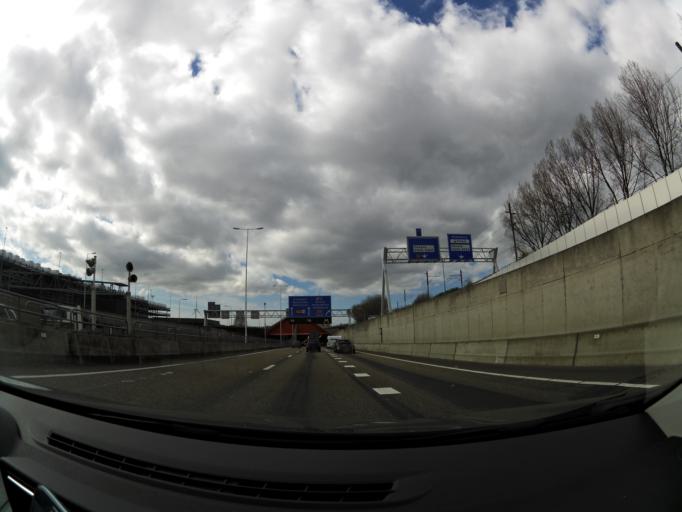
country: NL
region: South Holland
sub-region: Gemeente Maassluis
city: Maassluis
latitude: 51.8996
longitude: 4.2377
